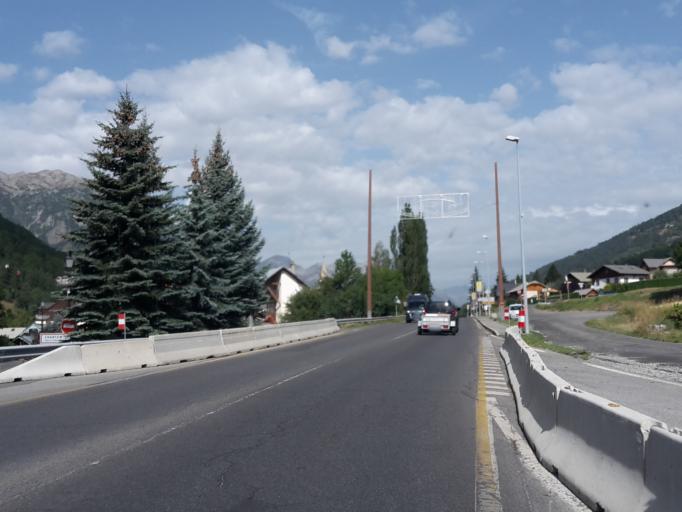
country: FR
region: Provence-Alpes-Cote d'Azur
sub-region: Departement des Hautes-Alpes
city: Saint-Chaffrey
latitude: 44.9307
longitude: 6.5932
